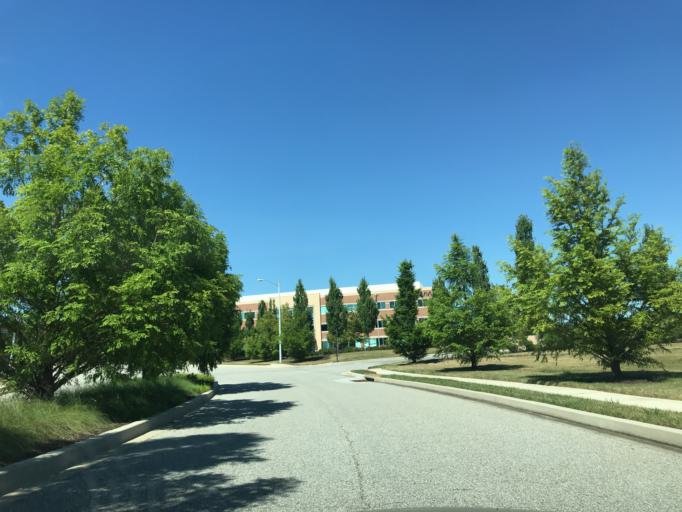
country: US
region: Maryland
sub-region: Harford County
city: Aberdeen
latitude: 39.5020
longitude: -76.1488
